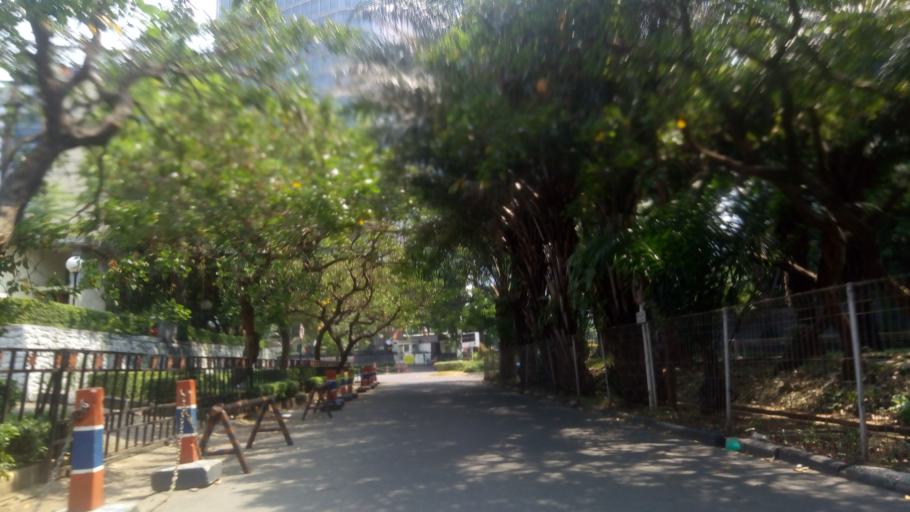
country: ID
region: Jakarta Raya
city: Jakarta
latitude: -6.2363
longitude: 106.8305
